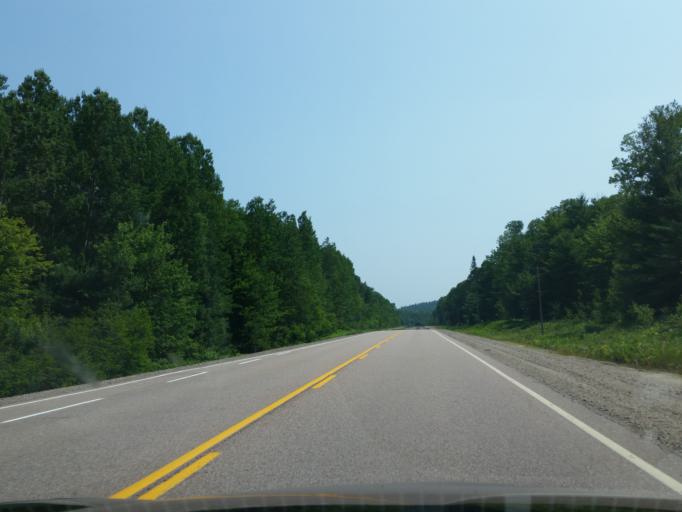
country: CA
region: Ontario
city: Deep River
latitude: 46.1745
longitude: -77.7822
